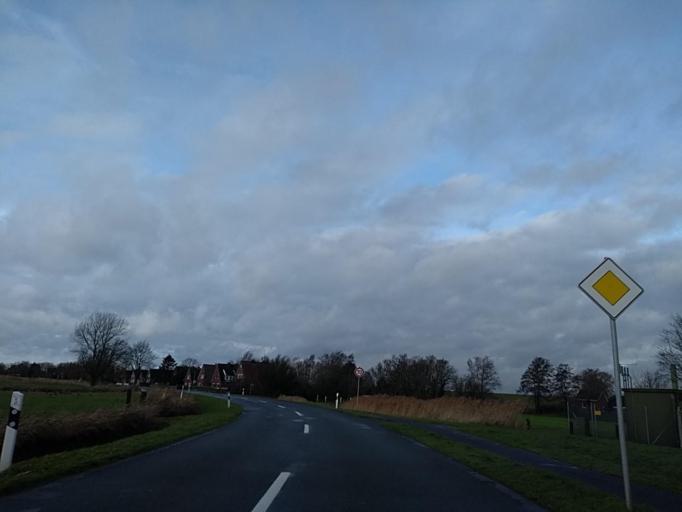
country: DE
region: Lower Saxony
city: Emden
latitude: 53.3163
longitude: 7.2730
